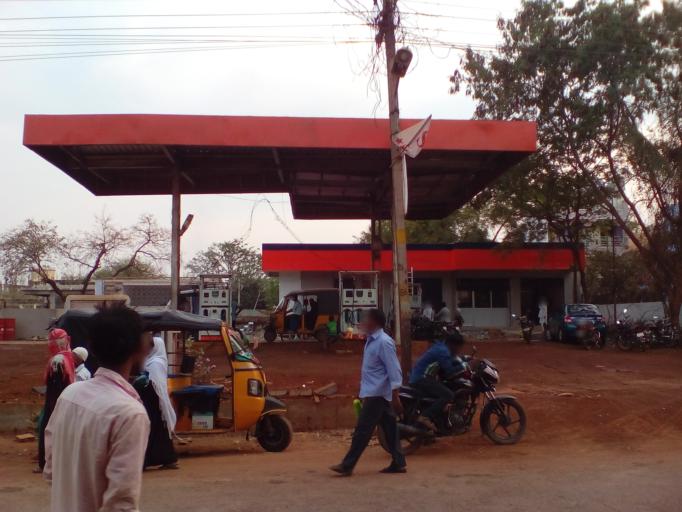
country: IN
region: Andhra Pradesh
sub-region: Kurnool
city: Nandikotkur
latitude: 15.8556
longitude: 78.2667
